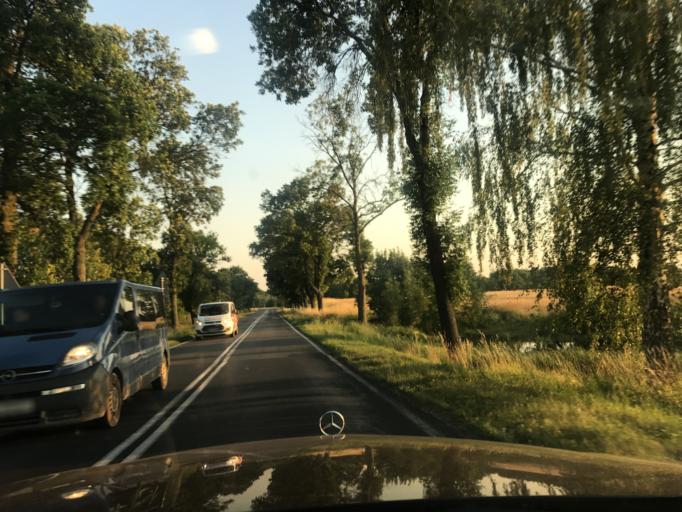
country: PL
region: Lublin Voivodeship
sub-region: Powiat lubartowski
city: Niedzwiada
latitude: 51.5037
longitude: 22.6610
